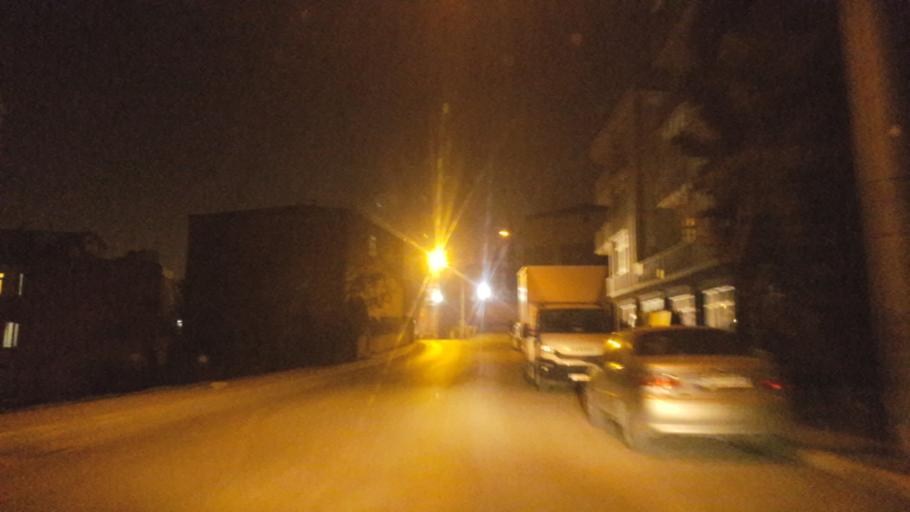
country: TR
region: Kocaeli
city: Tavsancil
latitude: 40.7836
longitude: 29.5438
